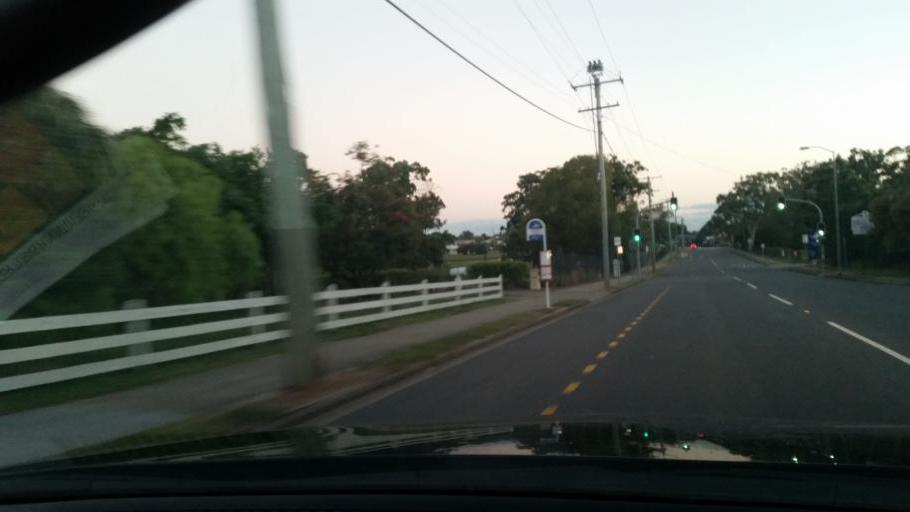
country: AU
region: Queensland
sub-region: Logan
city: Rochedale South
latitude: -27.5842
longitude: 153.1245
